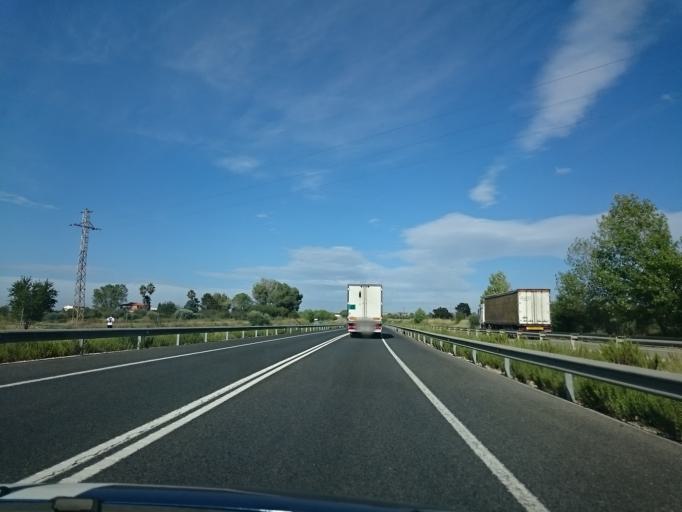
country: ES
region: Catalonia
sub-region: Provincia de Barcelona
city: Castellet
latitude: 41.3081
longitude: 1.6365
